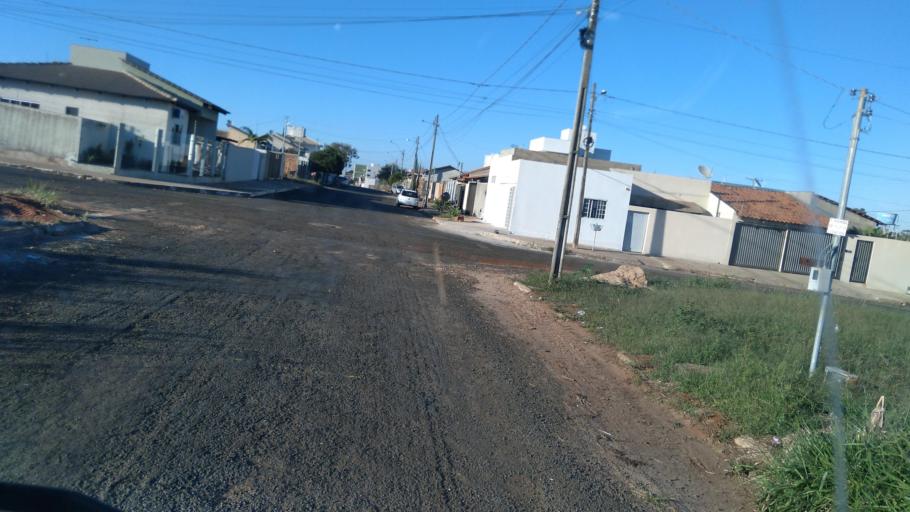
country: BR
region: Goias
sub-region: Mineiros
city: Mineiros
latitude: -17.5452
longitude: -52.5562
